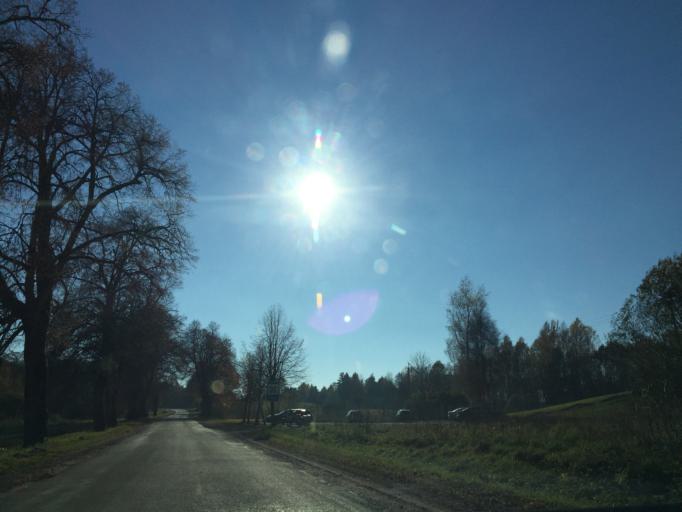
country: LT
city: Plateliai
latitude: 56.0325
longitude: 21.8099
